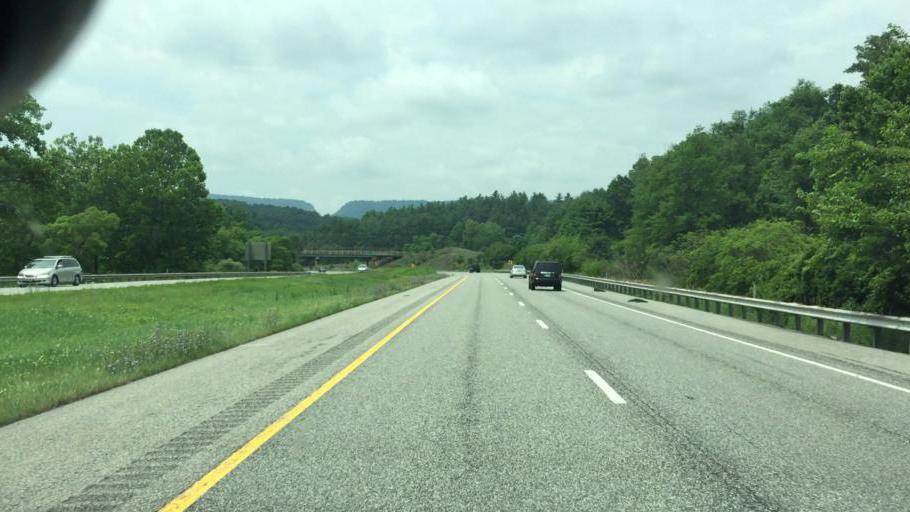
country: US
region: Maryland
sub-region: Washington County
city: Hancock
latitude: 39.7126
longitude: -78.2251
